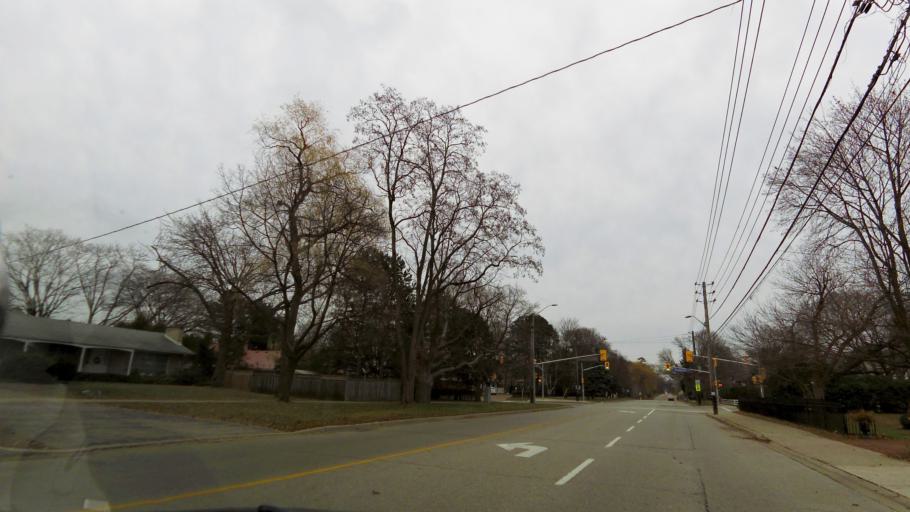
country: CA
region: Ontario
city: Mississauga
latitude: 43.5265
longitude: -79.6365
